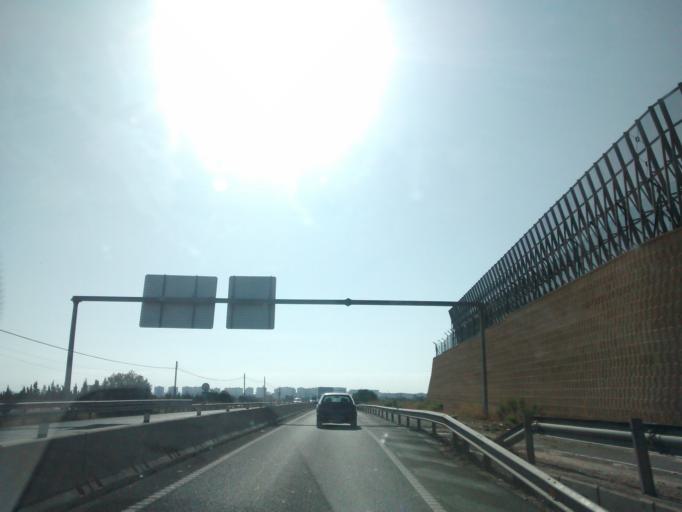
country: ES
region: Valencia
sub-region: Provincia de Alicante
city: Alicante
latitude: 38.2885
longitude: -0.5496
